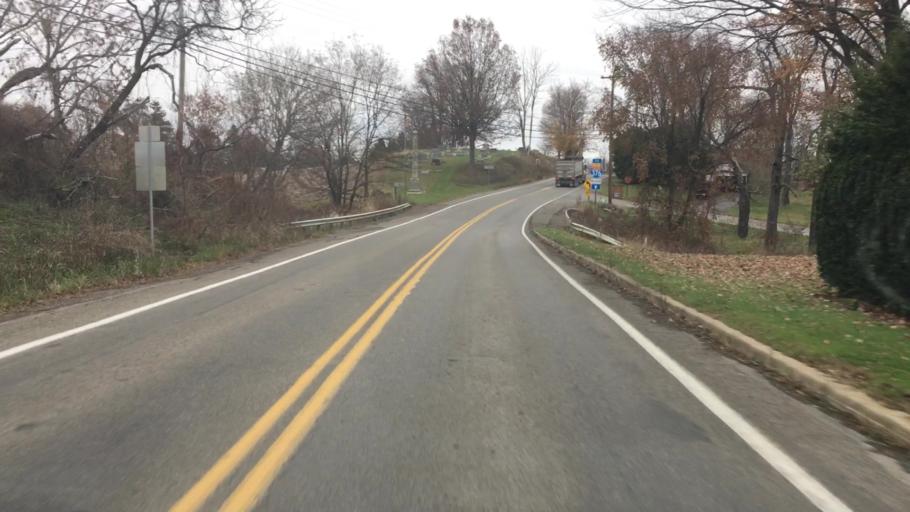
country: US
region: Pennsylvania
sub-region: Lawrence County
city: Bessemer
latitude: 40.9629
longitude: -80.4338
